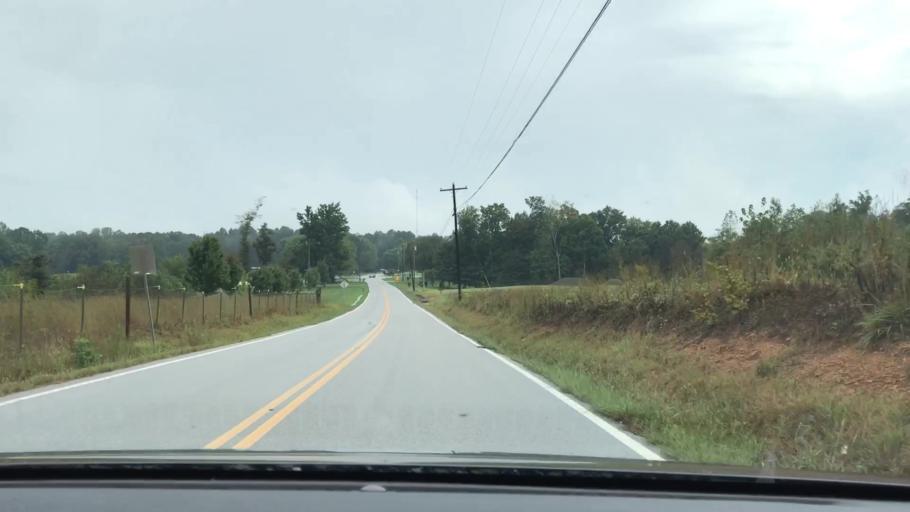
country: US
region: Tennessee
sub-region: Macon County
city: Red Boiling Springs
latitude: 36.4438
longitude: -85.8832
